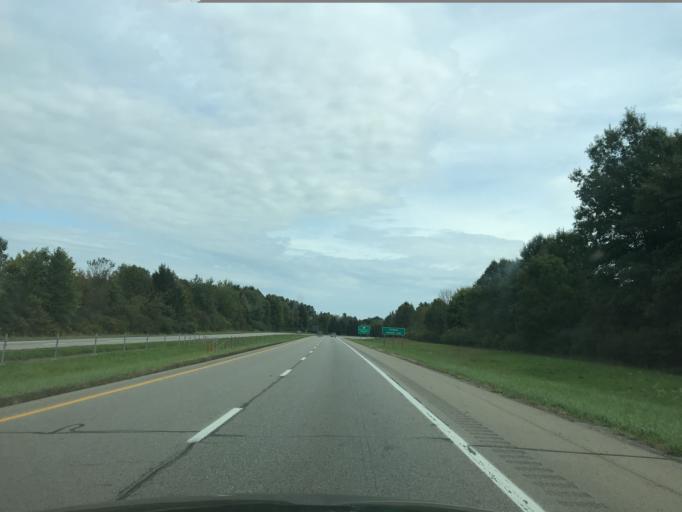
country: US
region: Ohio
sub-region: Trumbull County
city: Champion Heights
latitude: 41.2718
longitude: -80.8633
